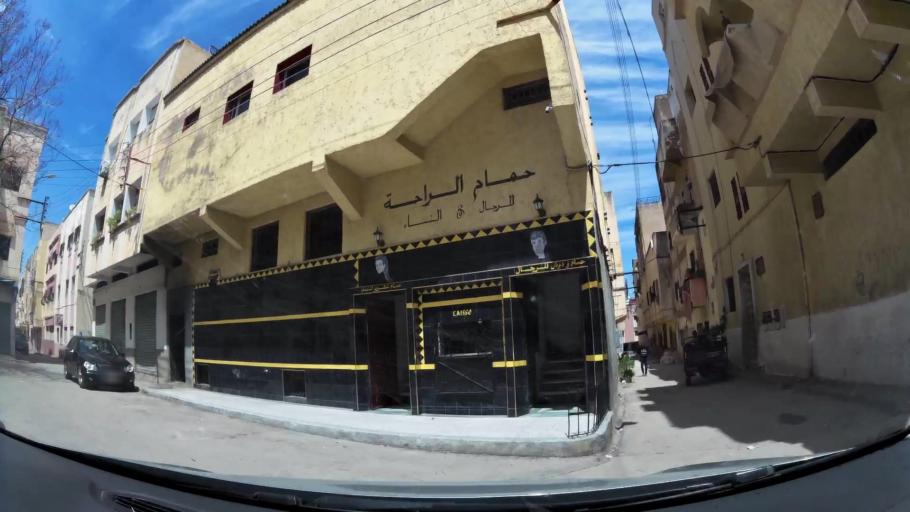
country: MA
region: Fes-Boulemane
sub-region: Fes
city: Fes
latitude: 34.0092
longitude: -4.9869
